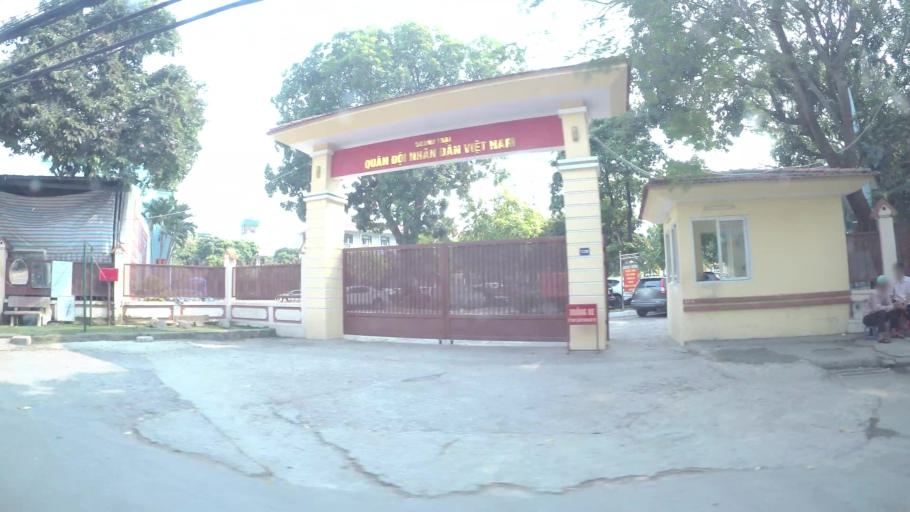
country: VN
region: Ha Noi
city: Dong Da
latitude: 20.9970
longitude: 105.8244
